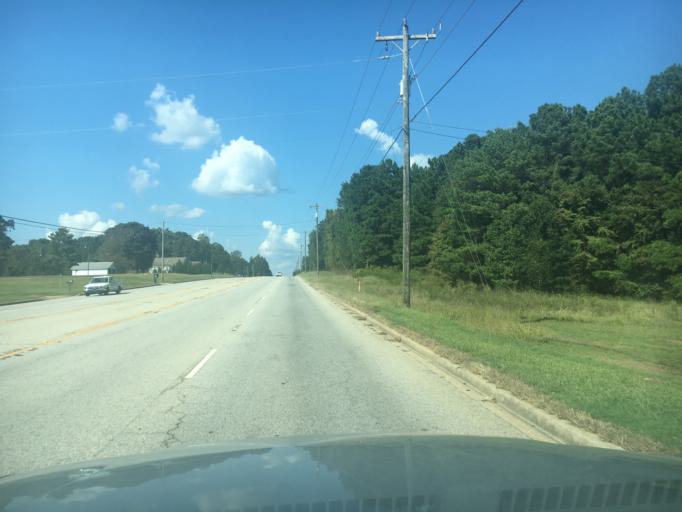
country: US
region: South Carolina
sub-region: Greenwood County
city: Ware Shoals
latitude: 34.3373
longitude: -82.2223
